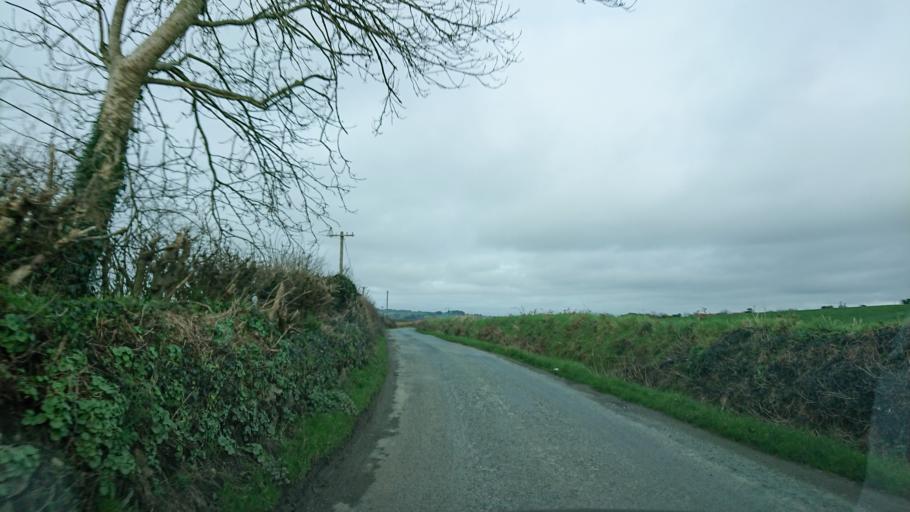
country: IE
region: Munster
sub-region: Waterford
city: Portlaw
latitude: 52.1772
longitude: -7.3033
